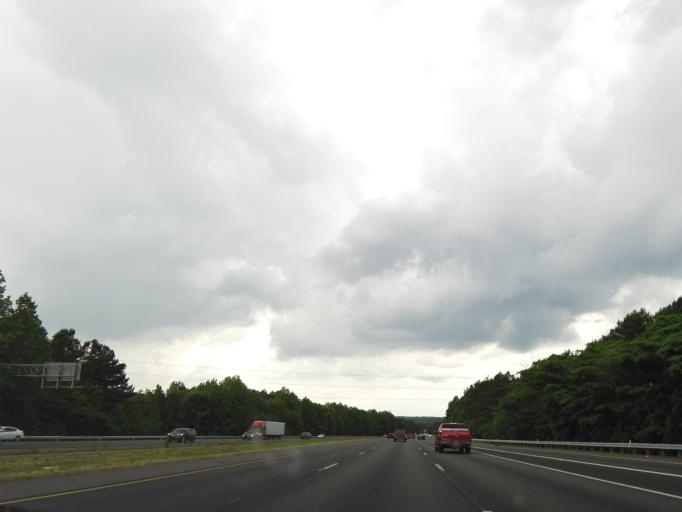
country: US
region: Georgia
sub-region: Carroll County
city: Villa Rica
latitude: 33.7197
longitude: -84.8375
